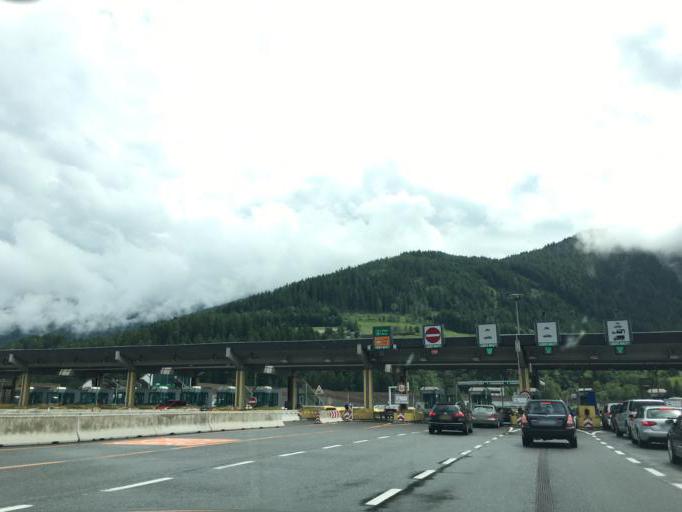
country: AT
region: Salzburg
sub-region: Politischer Bezirk Tamsweg
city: Sankt Michael im Lungau
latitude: 47.0944
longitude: 13.6091
